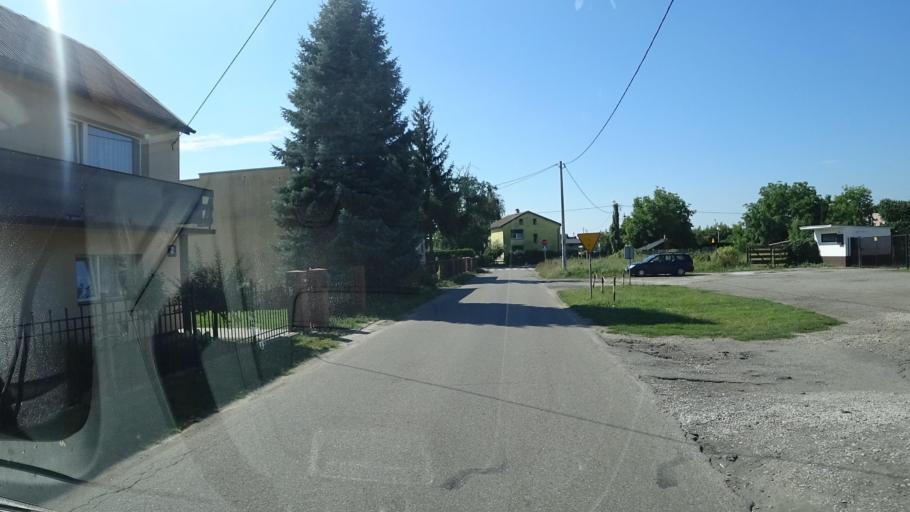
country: PL
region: Greater Poland Voivodeship
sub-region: Powiat koninski
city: Slesin
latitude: 52.3733
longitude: 18.3227
